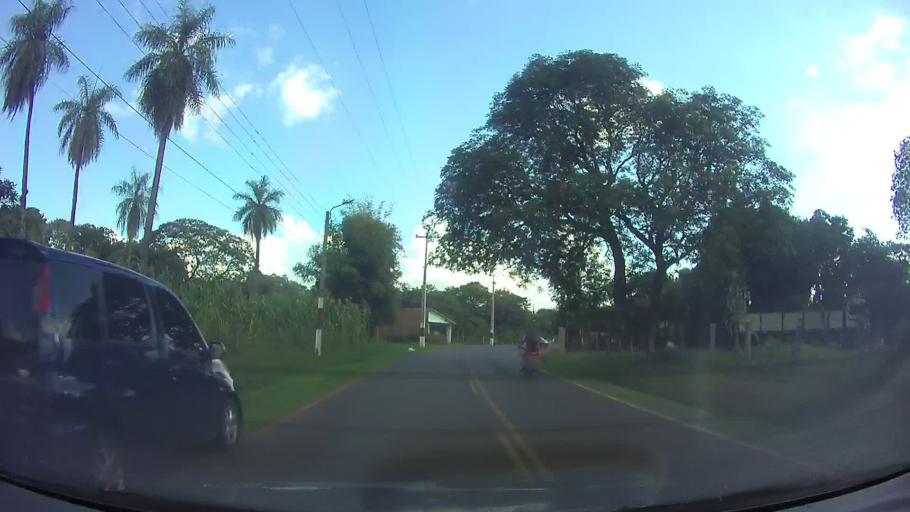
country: PY
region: Central
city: Aregua
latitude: -25.2741
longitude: -57.4300
